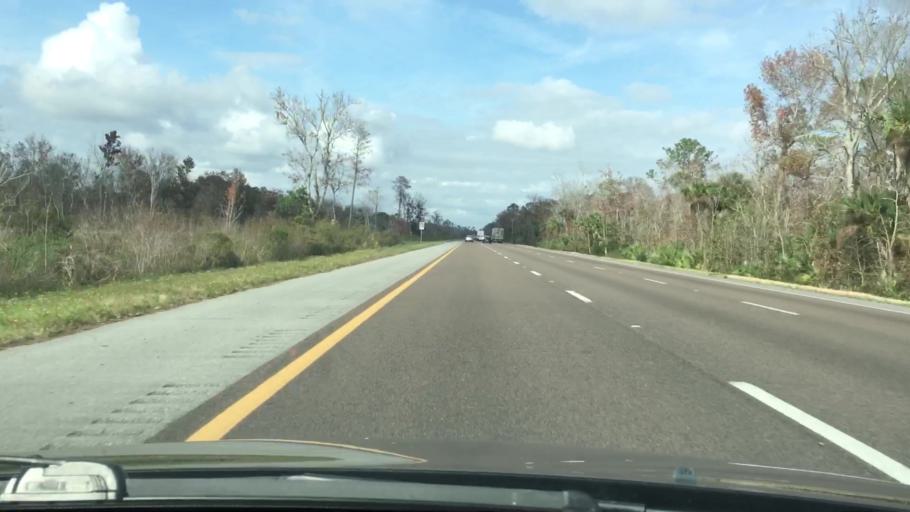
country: US
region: Florida
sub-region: Volusia County
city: Oak Hill
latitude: 28.8919
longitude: -80.9276
